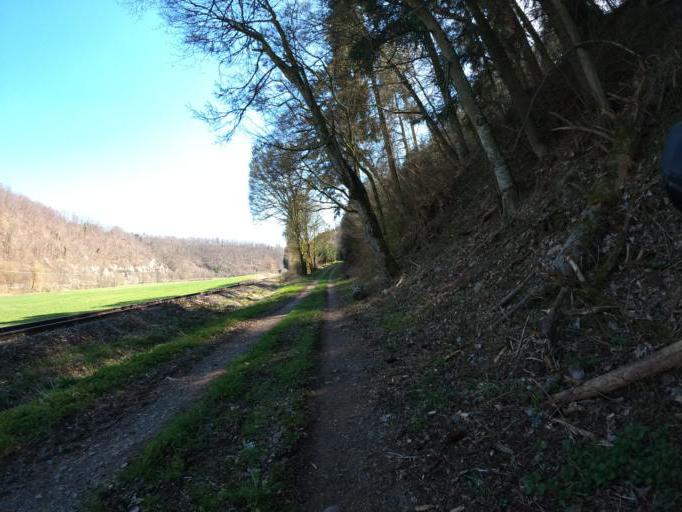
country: DE
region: Baden-Wuerttemberg
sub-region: Tuebingen Region
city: Haigerloch
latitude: 48.3861
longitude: 8.7875
